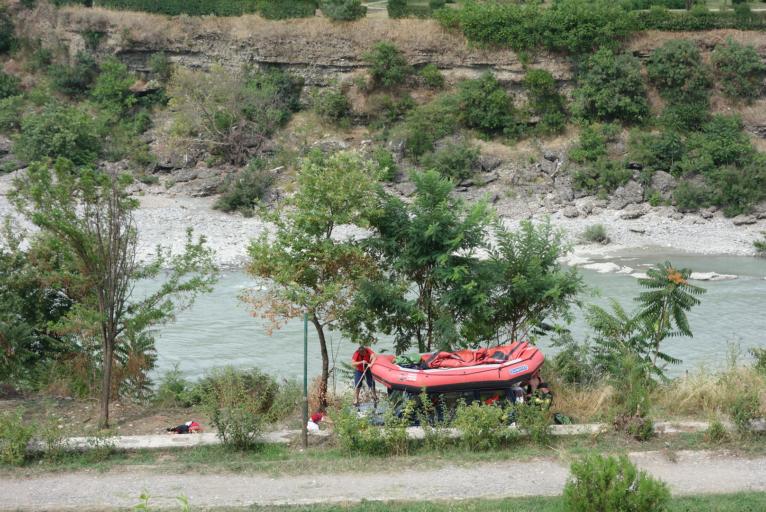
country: AL
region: Gjirokaster
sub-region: Rrethi i Permetit
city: Permet
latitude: 40.2341
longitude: 20.3528
